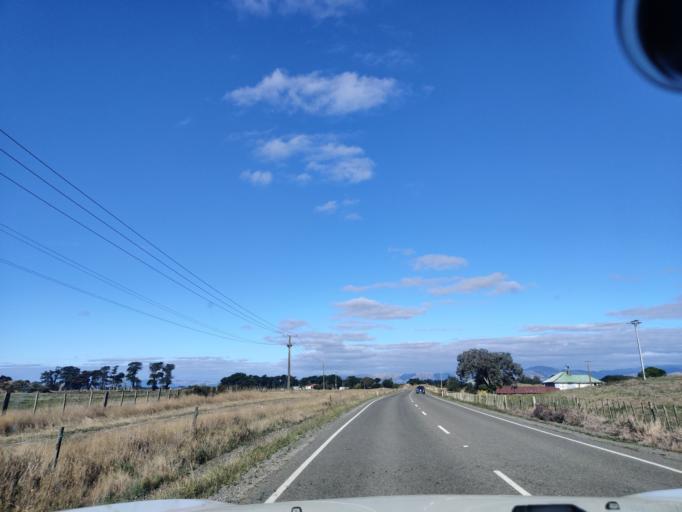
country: NZ
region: Manawatu-Wanganui
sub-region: Horowhenua District
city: Foxton
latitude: -40.4142
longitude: 175.3986
